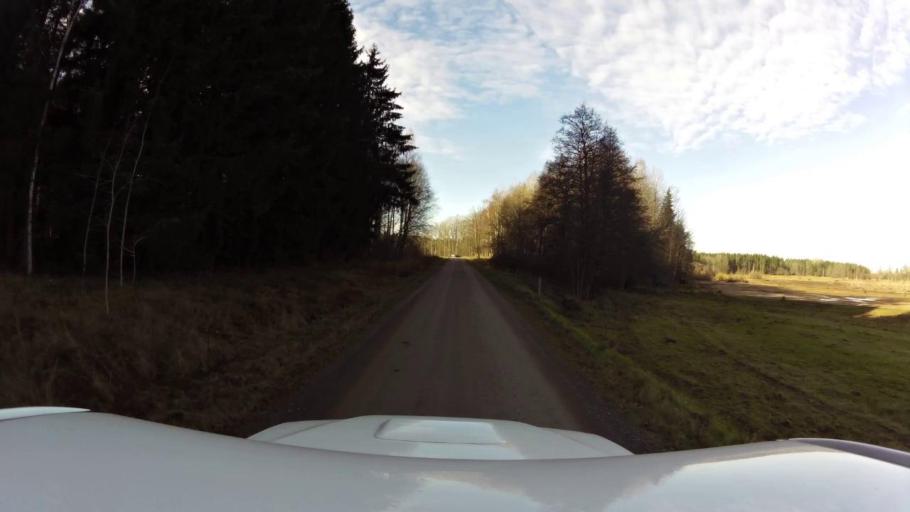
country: SE
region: OEstergoetland
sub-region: Linkopings Kommun
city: Linkoping
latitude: 58.3562
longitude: 15.6125
